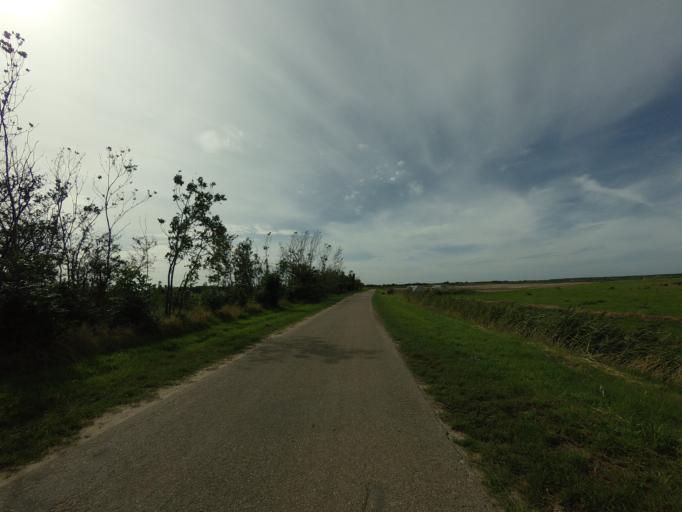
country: NL
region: North Holland
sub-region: Gemeente Texel
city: Den Burg
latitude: 53.0730
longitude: 4.7998
